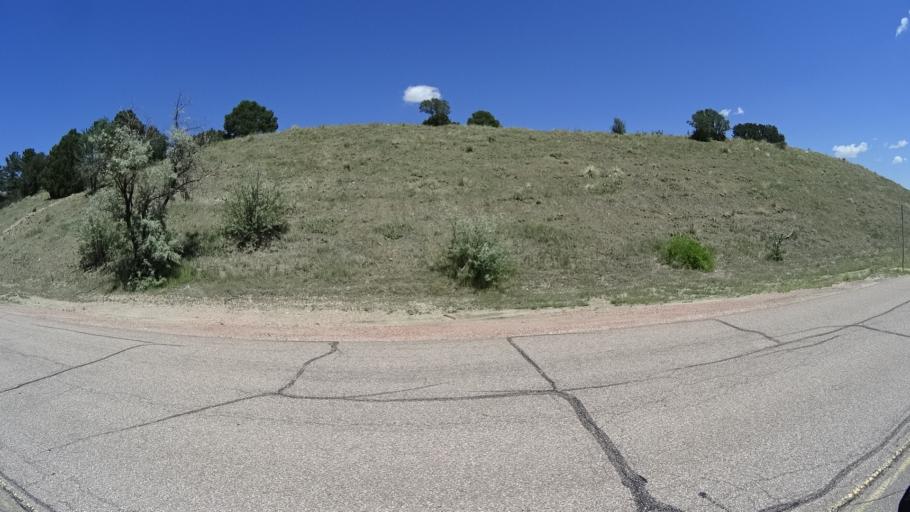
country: US
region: Colorado
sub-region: El Paso County
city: Colorado Springs
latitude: 38.9140
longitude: -104.8335
